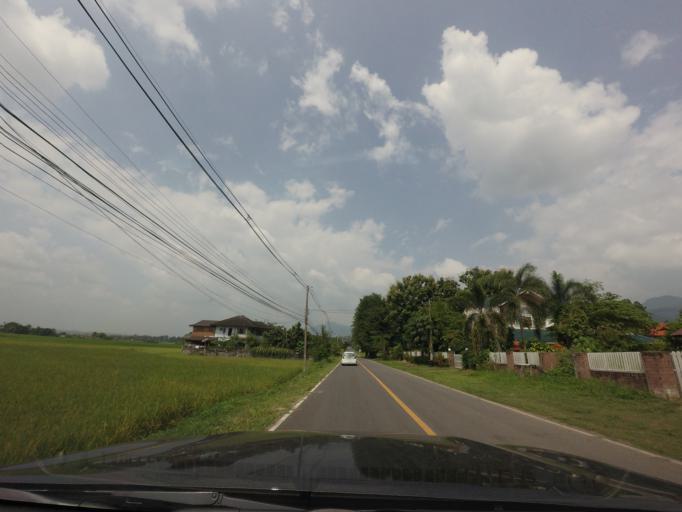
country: TH
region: Nan
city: Pua
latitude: 19.1747
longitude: 100.9419
